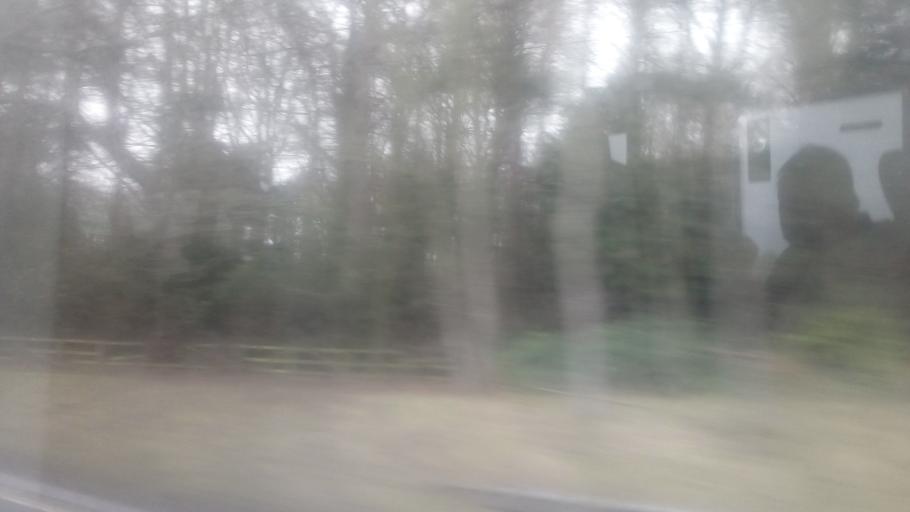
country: GB
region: Scotland
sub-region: The Scottish Borders
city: Newtown St Boswells
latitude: 55.5932
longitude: -2.6703
